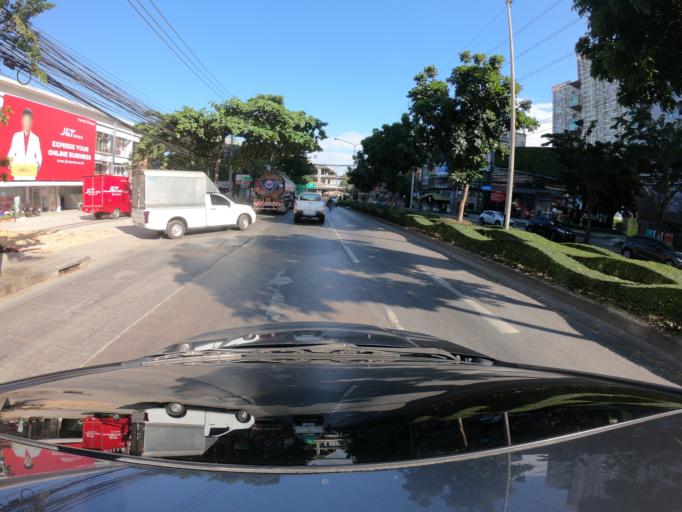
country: TH
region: Bangkok
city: Phra Khanong
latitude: 13.6736
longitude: 100.6045
